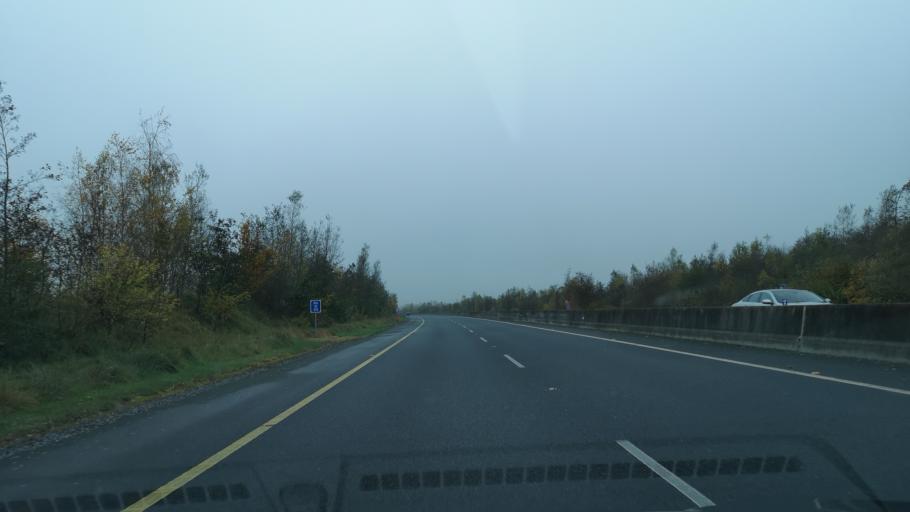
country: IE
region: Connaught
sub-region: County Galway
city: Ballinasloe
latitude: 53.3070
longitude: -8.3226
